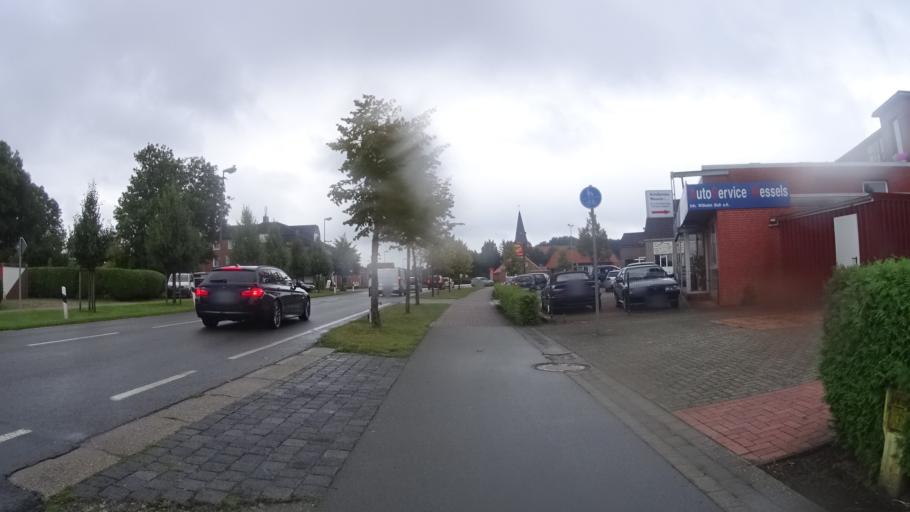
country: DE
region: Lower Saxony
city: Bunde
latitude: 53.1769
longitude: 7.3013
